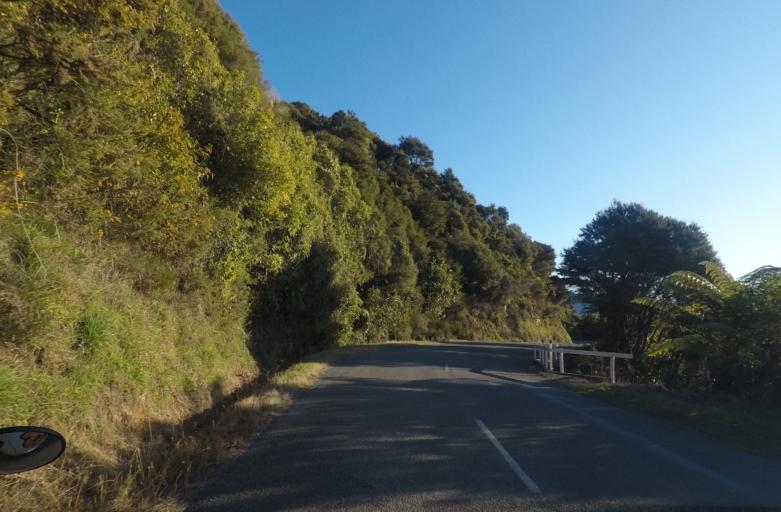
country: NZ
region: Marlborough
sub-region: Marlborough District
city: Picton
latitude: -41.2690
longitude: 173.9721
